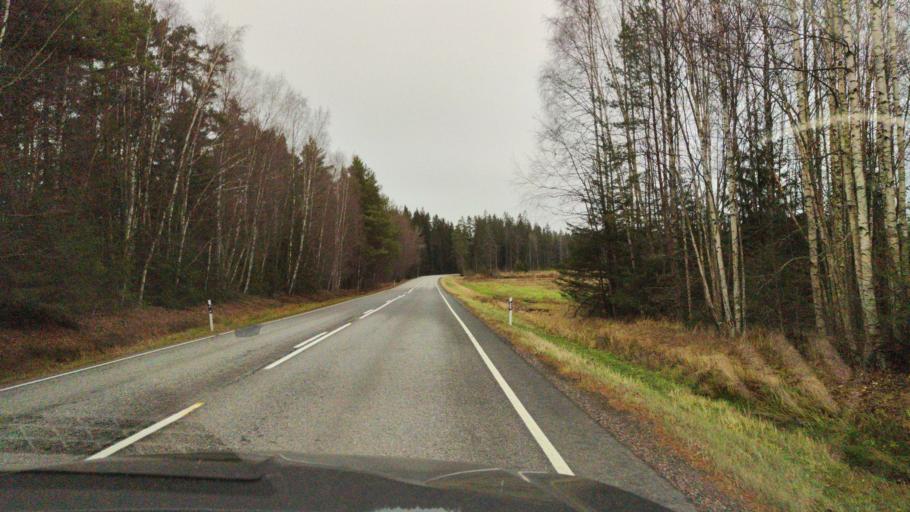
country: FI
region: Varsinais-Suomi
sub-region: Loimaa
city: Ylaene
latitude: 60.7511
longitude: 22.4272
